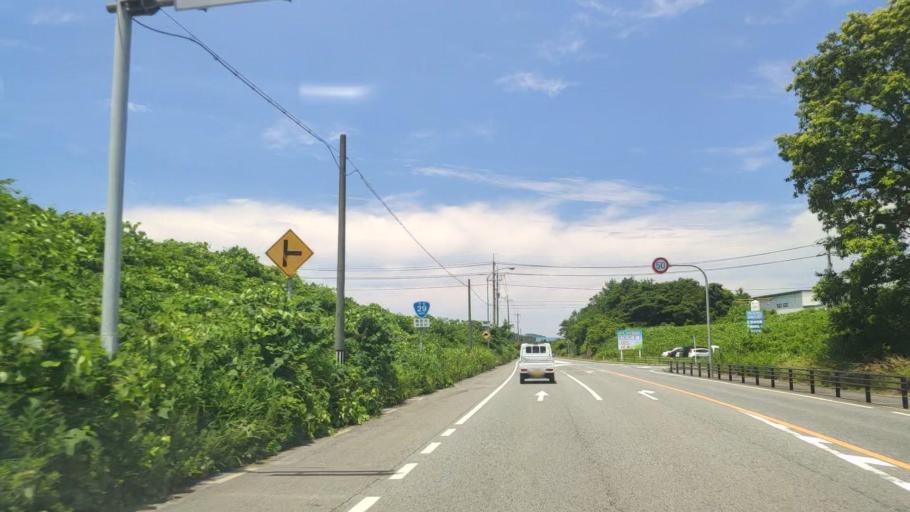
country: JP
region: Tottori
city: Tottori
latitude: 35.4366
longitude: 134.2569
